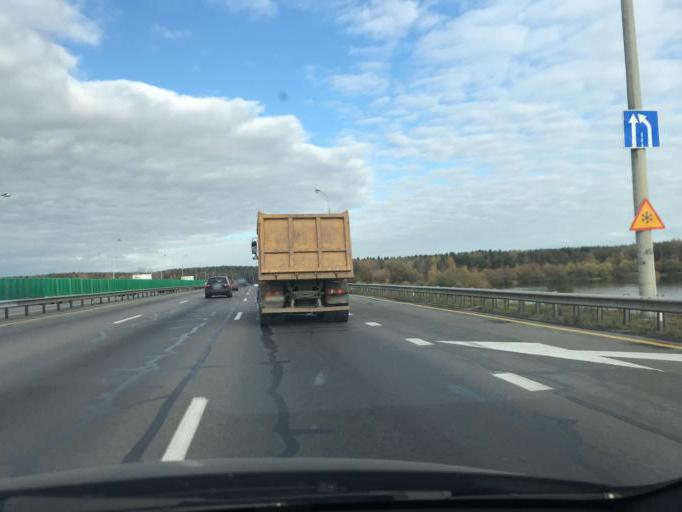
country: BY
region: Minsk
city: Zhdanovichy
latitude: 53.9568
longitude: 27.4536
